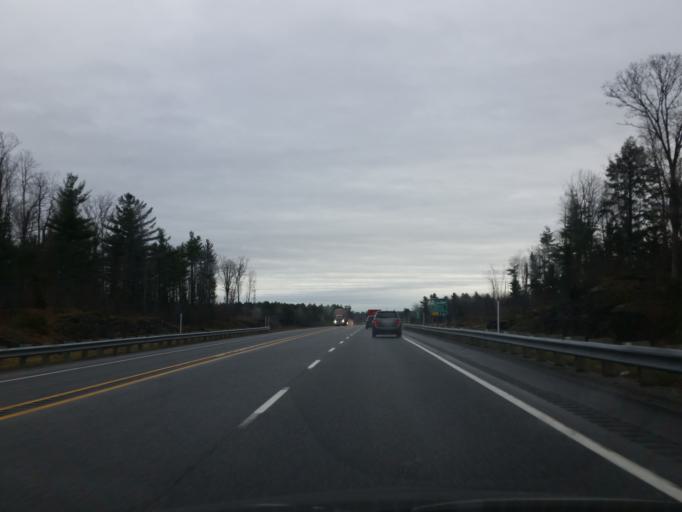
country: CA
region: Quebec
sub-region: Outaouais
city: Thurso
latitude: 45.6221
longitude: -75.2665
